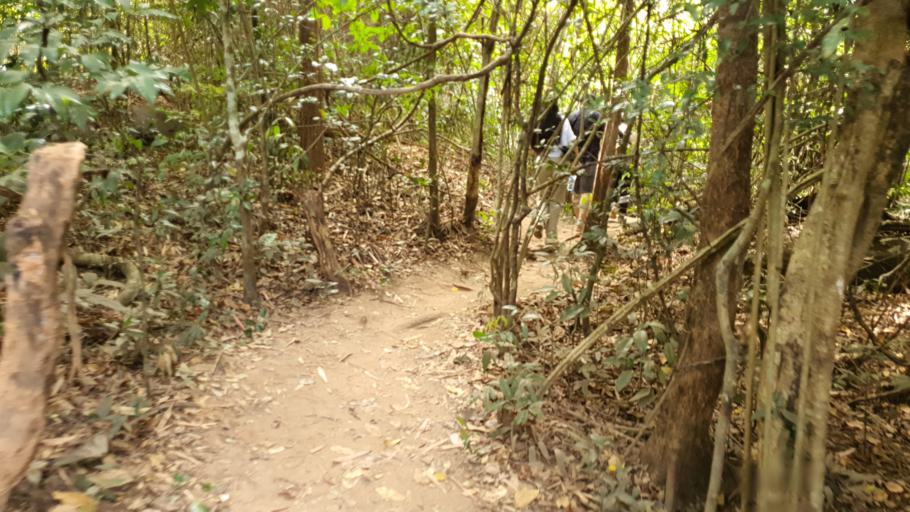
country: TH
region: Changwat Bueng Kan
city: Bueng Khong Long
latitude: 17.9844
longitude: 104.1294
